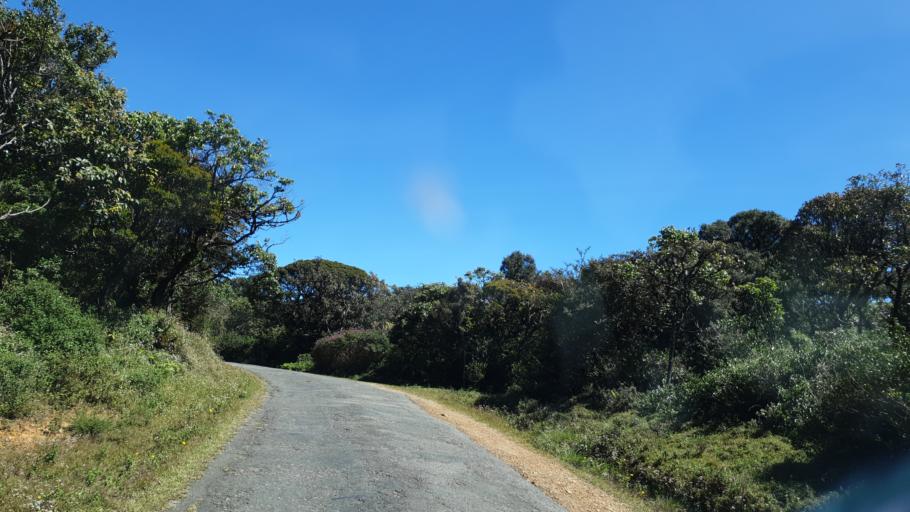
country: LK
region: Central
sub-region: Nuwara Eliya District
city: Nuwara Eliya
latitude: 6.8267
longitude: 80.8060
